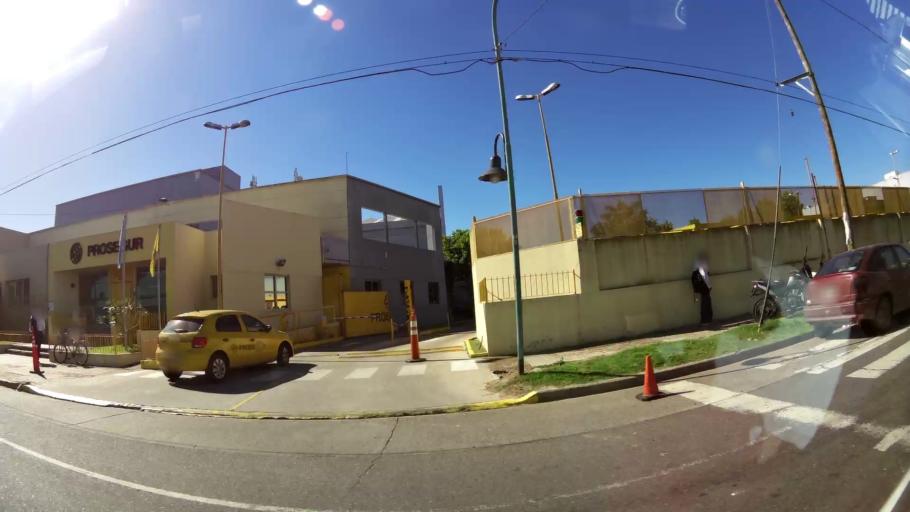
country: AR
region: Buenos Aires
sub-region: Partido de General San Martin
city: General San Martin
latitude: -34.5437
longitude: -58.5175
